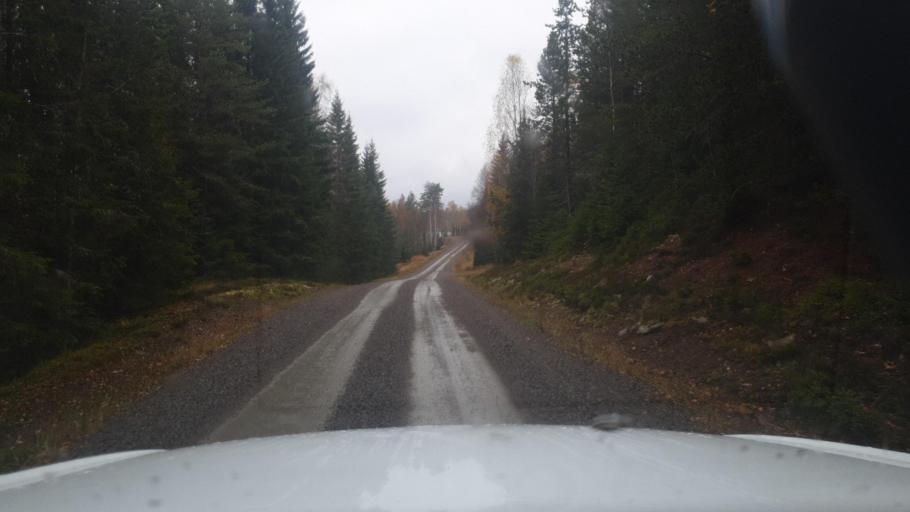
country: SE
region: Vaermland
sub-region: Eda Kommun
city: Charlottenberg
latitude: 60.1025
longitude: 12.6078
